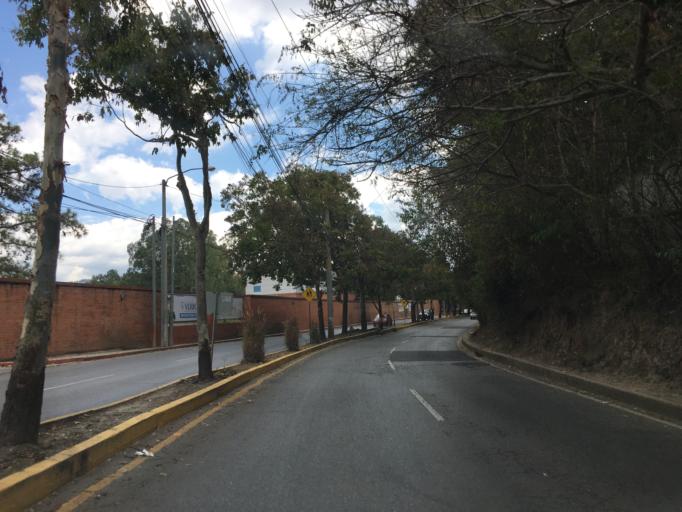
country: GT
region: Guatemala
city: Guatemala City
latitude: 14.6171
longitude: -90.4726
